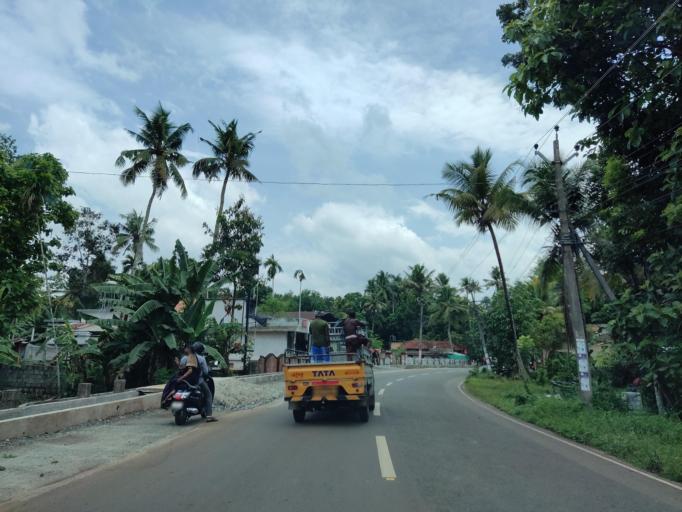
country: IN
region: Kerala
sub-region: Alappuzha
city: Mavelikara
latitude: 9.2259
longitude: 76.6207
